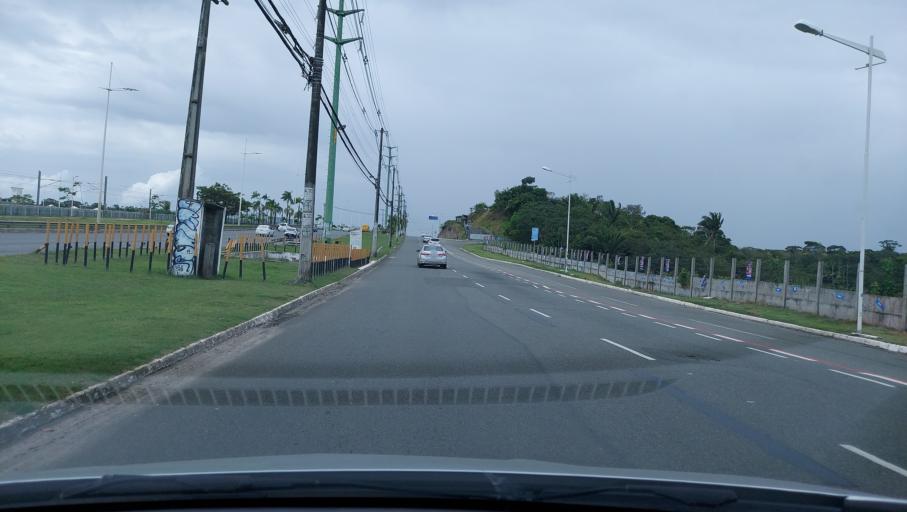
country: BR
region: Bahia
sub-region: Lauro De Freitas
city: Lauro de Freitas
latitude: -12.9303
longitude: -38.3885
